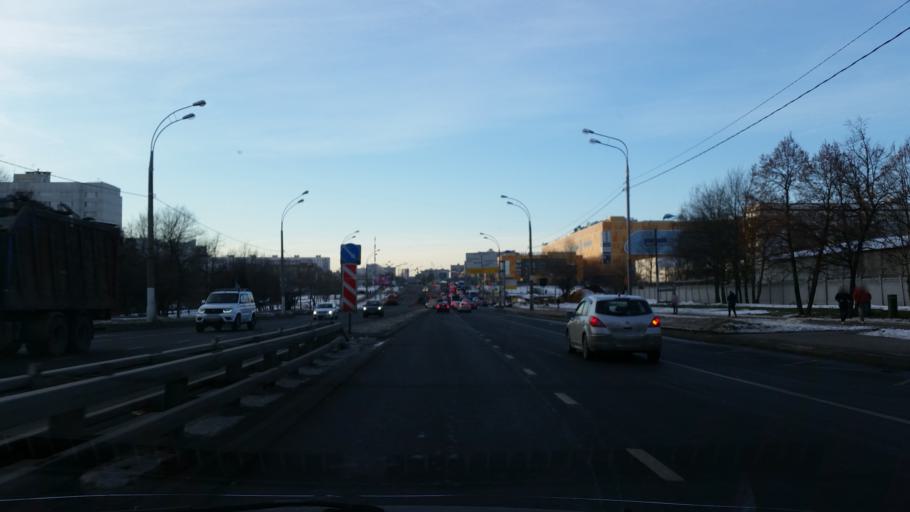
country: RU
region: Moscow
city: Chertanovo Yuzhnoye
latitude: 55.6092
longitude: 37.6148
